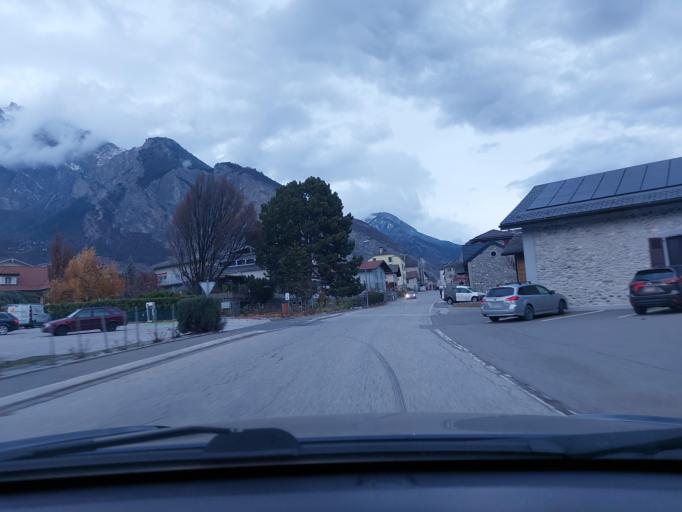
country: CH
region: Valais
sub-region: Conthey District
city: Chamoson
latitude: 46.1898
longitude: 7.2358
